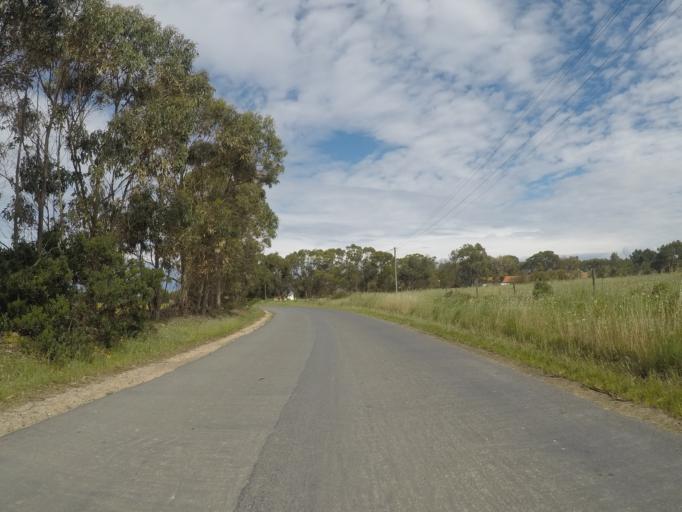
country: PT
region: Beja
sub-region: Odemira
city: Sao Teotonio
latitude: 37.4942
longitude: -8.7847
